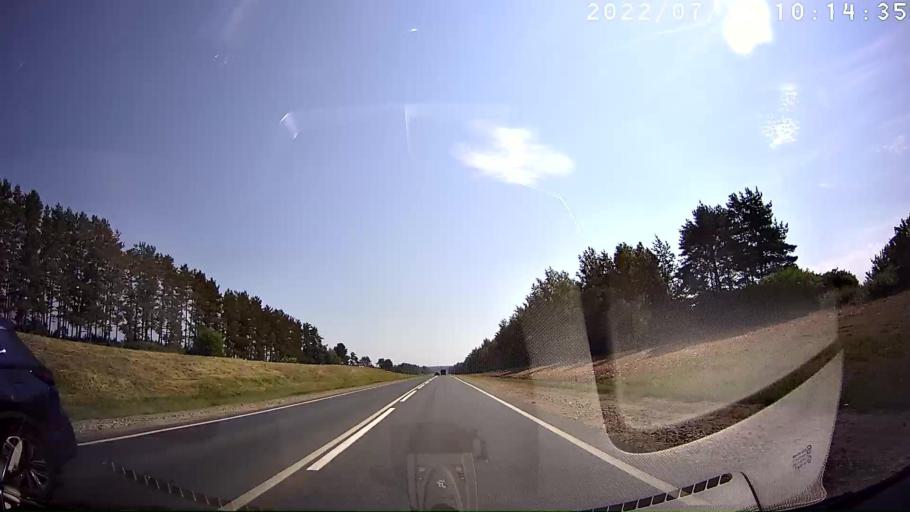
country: RU
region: Mariy-El
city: Sovetskiy
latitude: 56.7458
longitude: 48.2887
